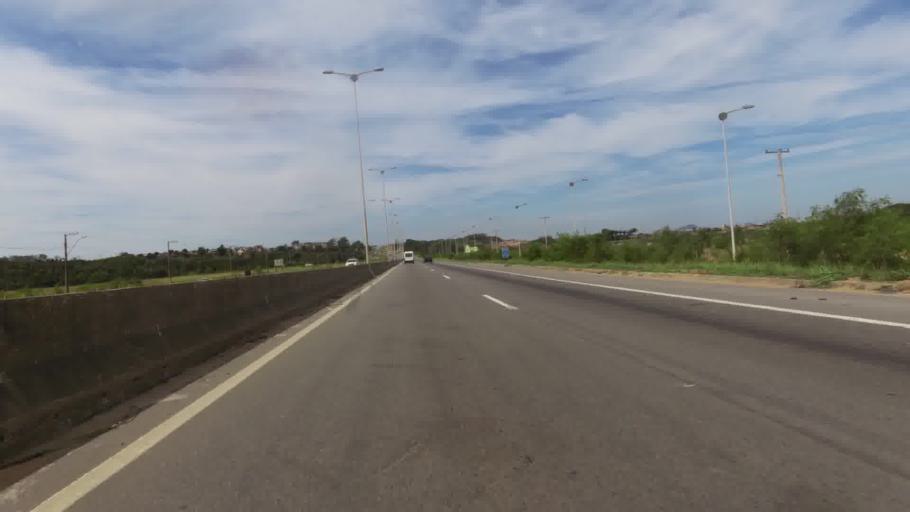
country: BR
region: Espirito Santo
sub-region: Serra
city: Serra
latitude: -20.2192
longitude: -40.2913
